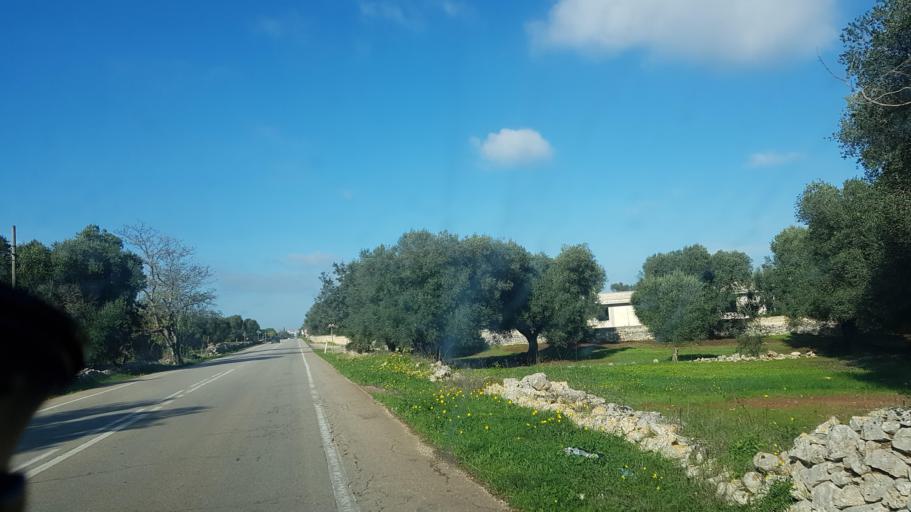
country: IT
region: Apulia
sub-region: Provincia di Brindisi
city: San Vito dei Normanni
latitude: 40.6742
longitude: 17.6904
